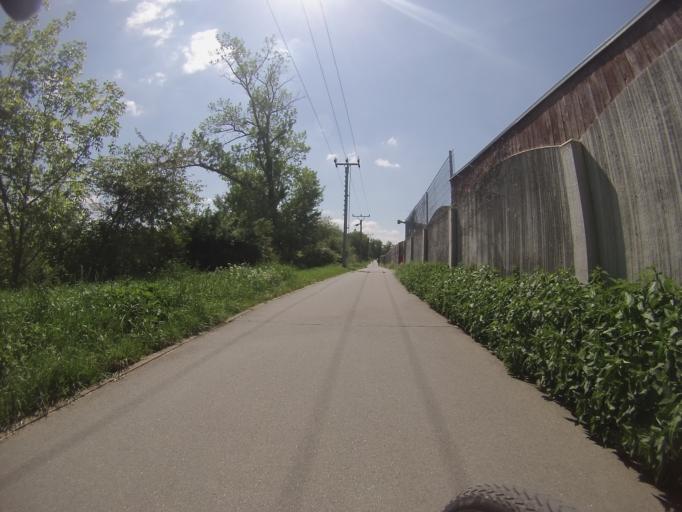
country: CZ
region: South Moravian
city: Modrice
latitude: 49.1517
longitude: 16.6274
